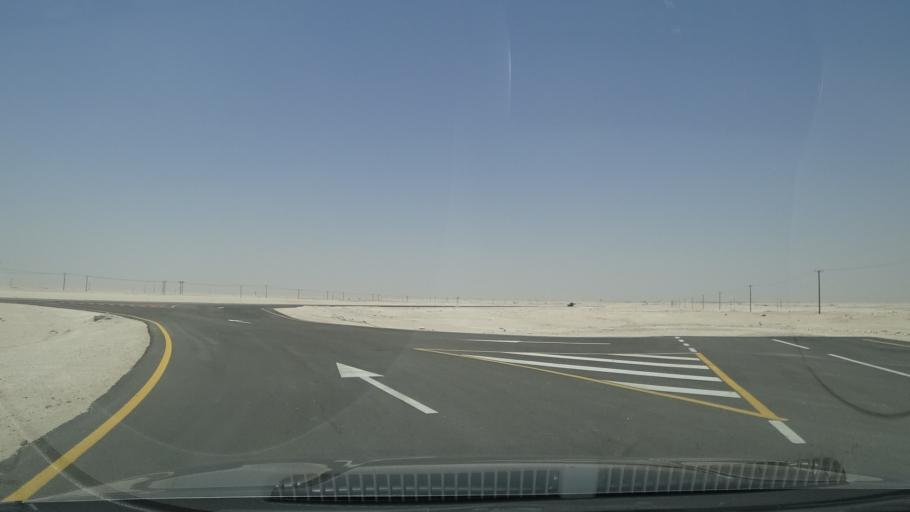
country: OM
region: Al Wusta
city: Hayma'
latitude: 19.9288
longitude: 56.2142
